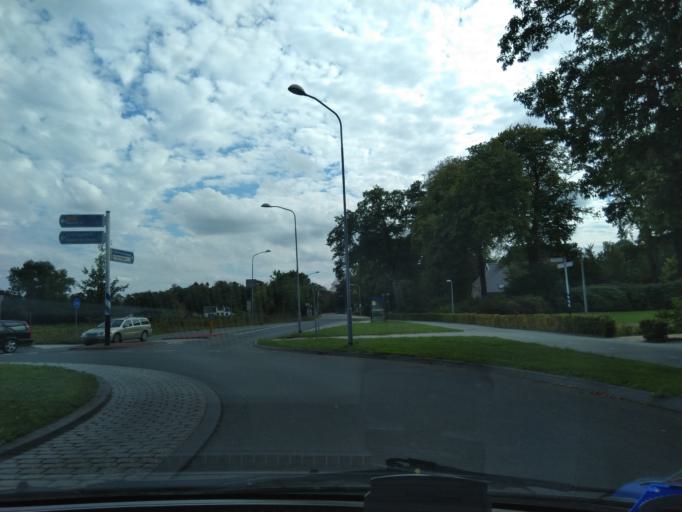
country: NL
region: Groningen
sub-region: Gemeente Haren
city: Haren
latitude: 53.1576
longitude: 6.5637
